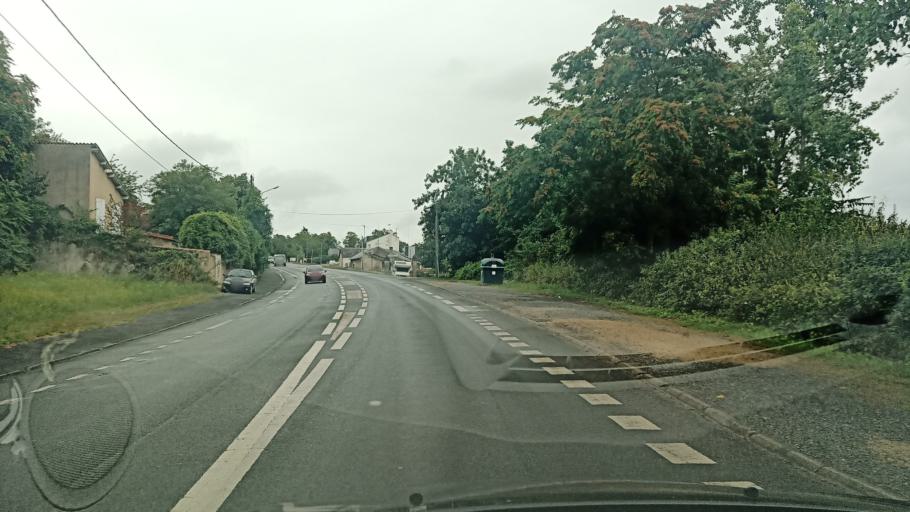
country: FR
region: Poitou-Charentes
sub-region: Departement de la Vienne
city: Poitiers
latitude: 46.6082
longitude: 0.3471
